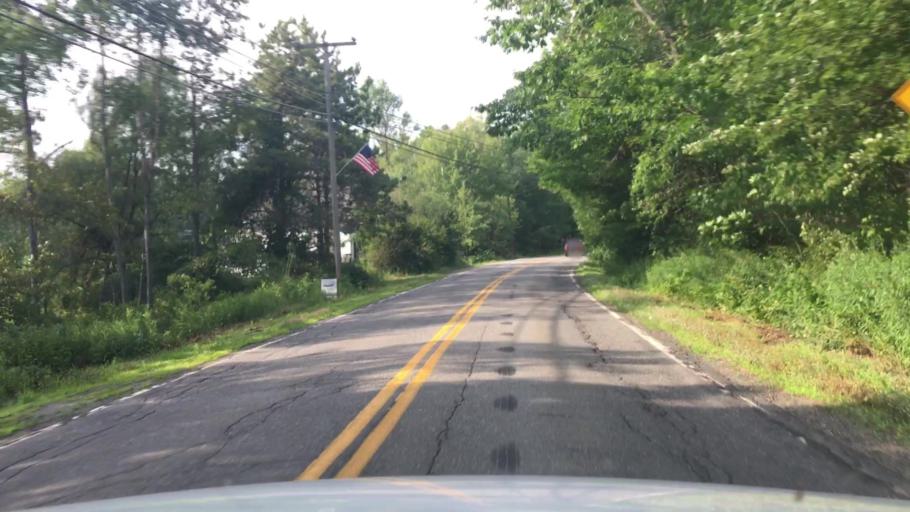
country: US
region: Maine
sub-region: Lincoln County
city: Waldoboro
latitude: 44.1019
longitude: -69.3697
